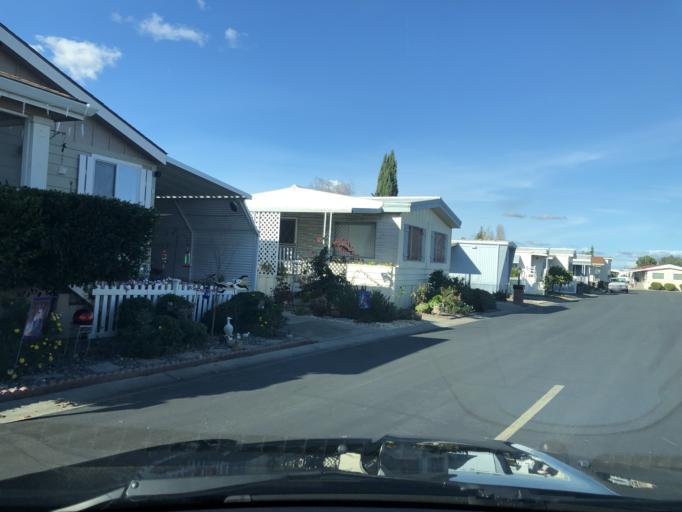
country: US
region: California
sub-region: Contra Costa County
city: Pacheco
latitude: 37.9929
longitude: -122.0639
